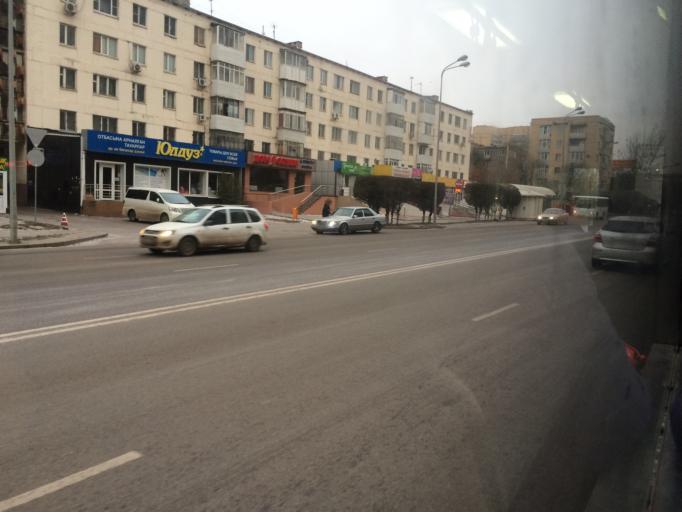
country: KZ
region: Astana Qalasy
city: Astana
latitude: 51.1677
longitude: 71.4399
